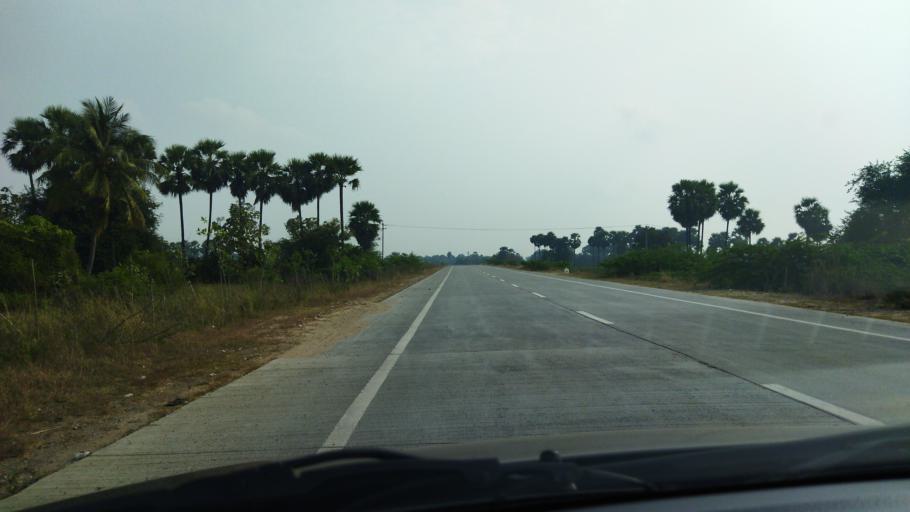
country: IN
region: Telangana
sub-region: Nalgonda
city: Nalgonda
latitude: 17.1832
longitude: 79.4150
